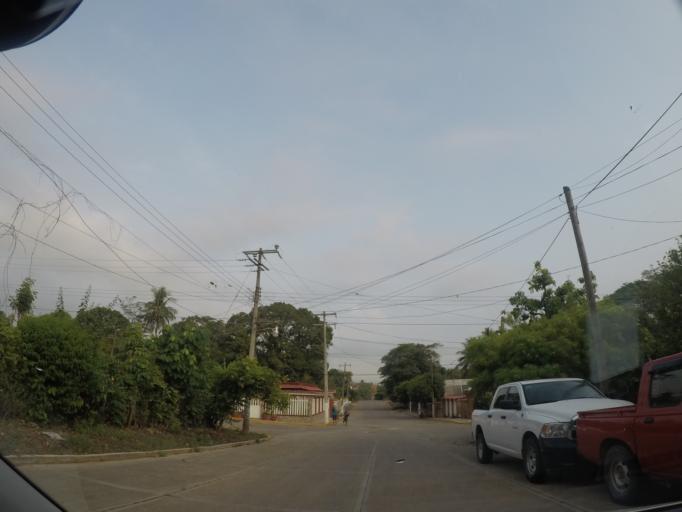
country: MX
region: Oaxaca
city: Matias Romero
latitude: 16.8714
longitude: -95.0420
